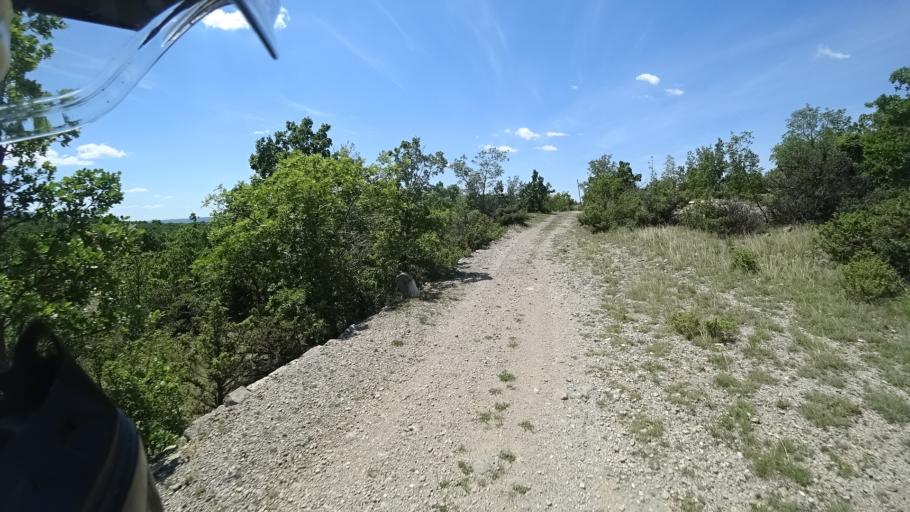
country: HR
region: Sibensko-Kniniska
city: Knin
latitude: 44.0334
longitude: 16.2400
